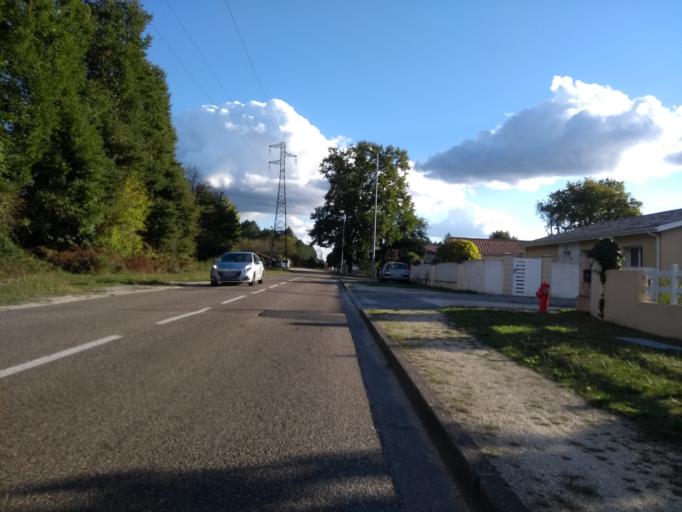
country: FR
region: Aquitaine
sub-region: Departement de la Gironde
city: Canejan
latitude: 44.7469
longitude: -0.6376
